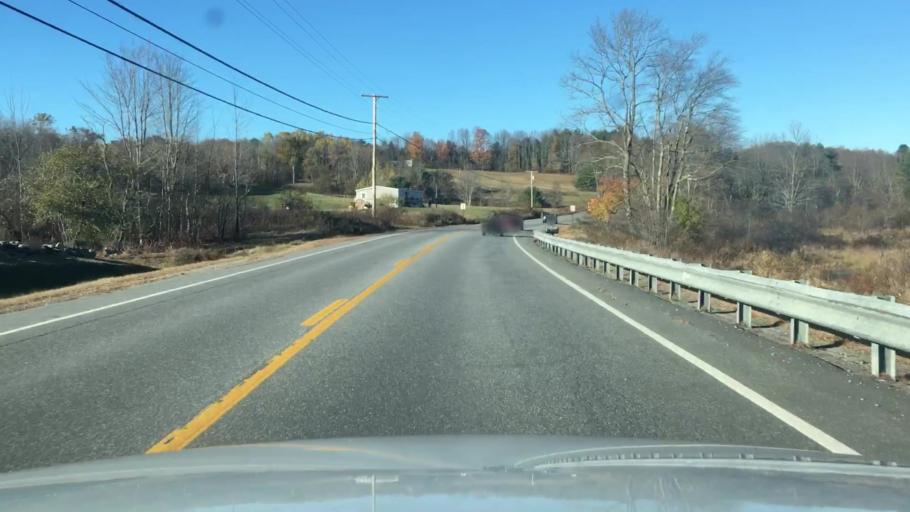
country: US
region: Maine
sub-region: Sagadahoc County
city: Topsham
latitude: 44.0351
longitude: -69.9435
